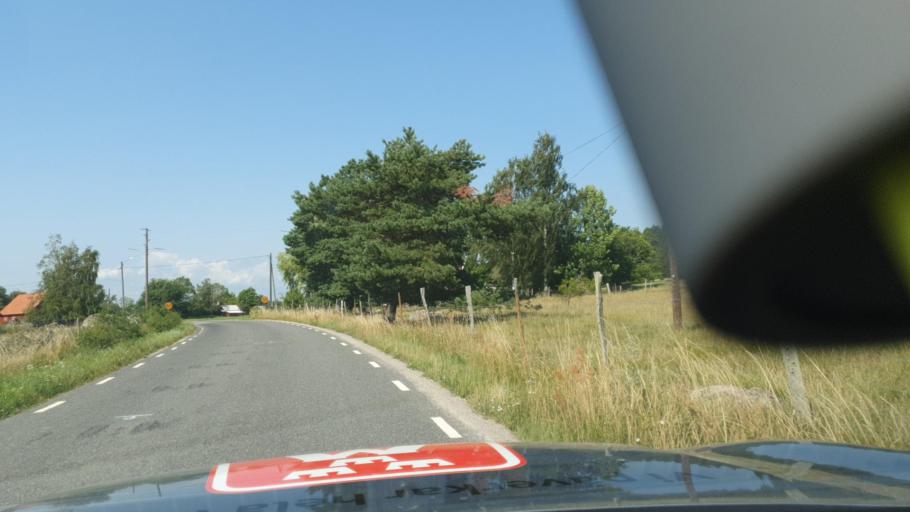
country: SE
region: Skane
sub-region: Kristianstads Kommun
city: Fjalkinge
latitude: 56.0696
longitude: 14.3611
